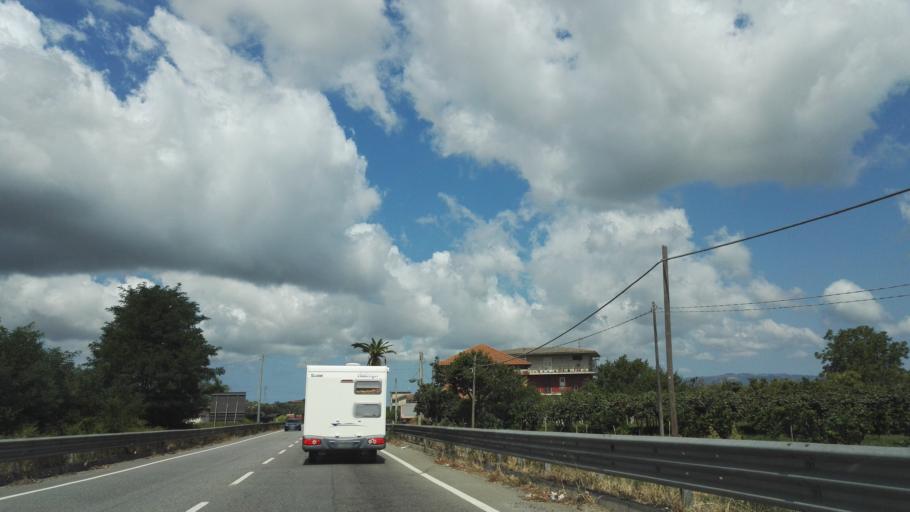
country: IT
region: Calabria
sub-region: Provincia di Reggio Calabria
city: Melicucco
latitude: 38.4549
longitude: 16.0256
